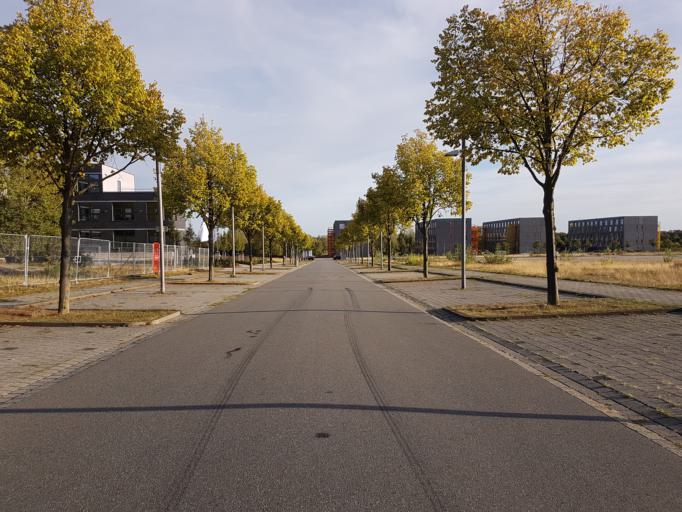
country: DE
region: Lower Saxony
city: Laatzen
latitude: 52.3158
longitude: 9.8213
